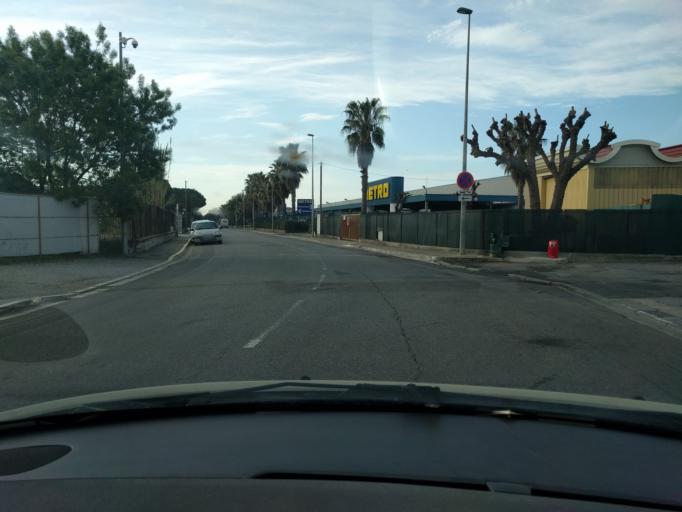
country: FR
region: Provence-Alpes-Cote d'Azur
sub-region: Departement des Alpes-Maritimes
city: Mandelieu-la-Napoule
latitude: 43.5490
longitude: 6.9651
